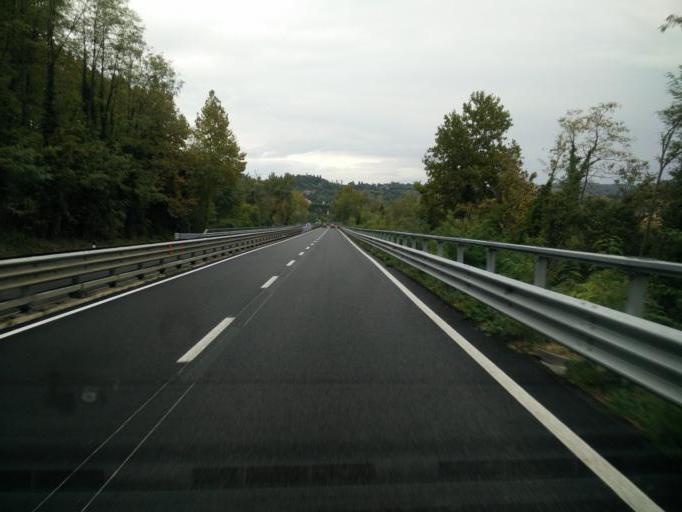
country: IT
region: Tuscany
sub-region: Provincia di Siena
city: Bellavista
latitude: 43.4416
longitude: 11.1501
